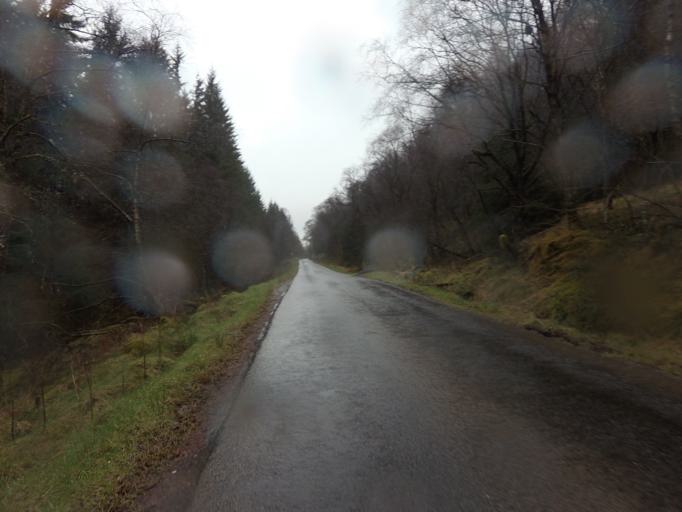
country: GB
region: Scotland
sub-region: West Dunbartonshire
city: Balloch
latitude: 56.2306
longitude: -4.5574
